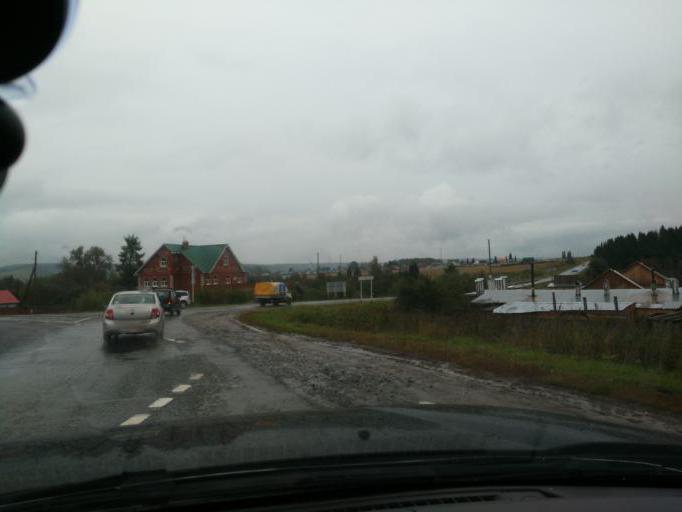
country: RU
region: Perm
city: Yugo-Kamskiy
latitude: 57.6876
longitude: 55.5673
